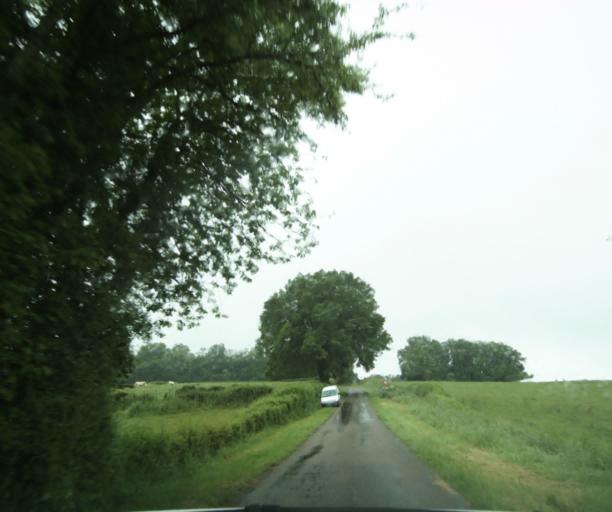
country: FR
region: Bourgogne
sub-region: Departement de Saone-et-Loire
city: Charolles
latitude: 46.4456
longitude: 4.2097
